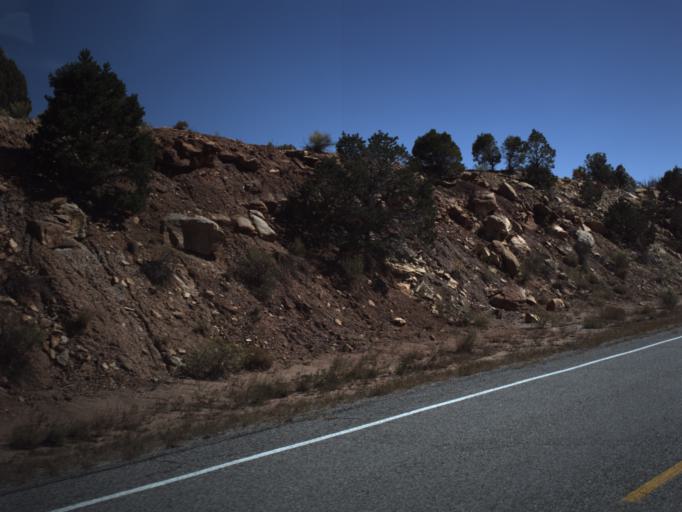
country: US
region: Utah
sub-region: San Juan County
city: Blanding
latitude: 37.5850
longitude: -109.8941
